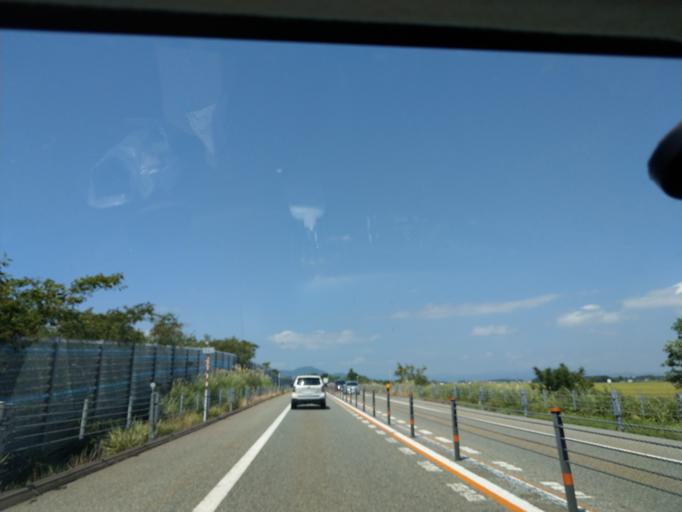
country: JP
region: Akita
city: Omagari
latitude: 39.3777
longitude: 140.4817
